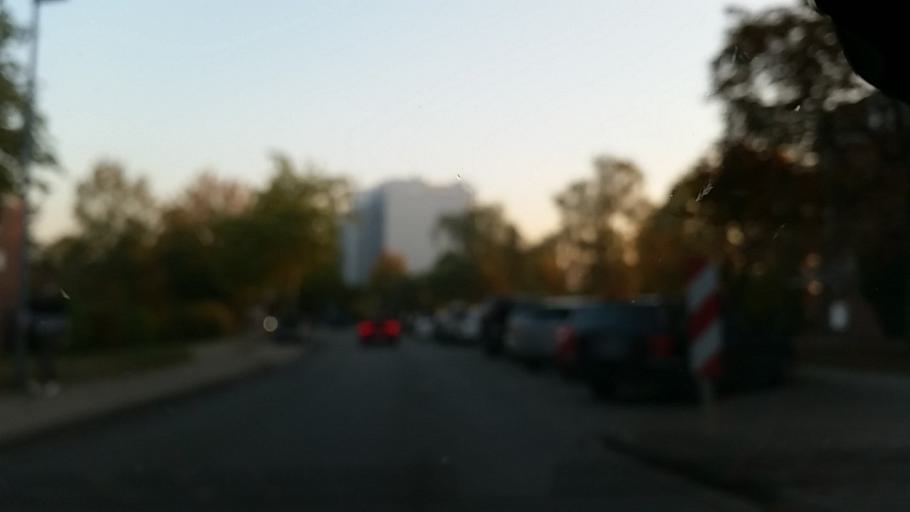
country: DE
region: Lower Saxony
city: Wolfsburg
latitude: 52.3981
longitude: 10.7386
